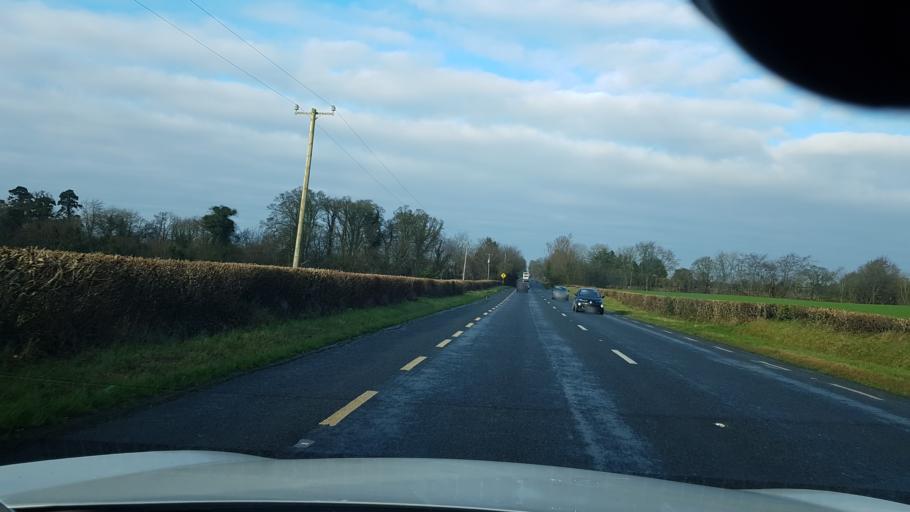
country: IE
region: Leinster
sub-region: An Mhi
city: Navan
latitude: 53.6152
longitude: -6.6368
